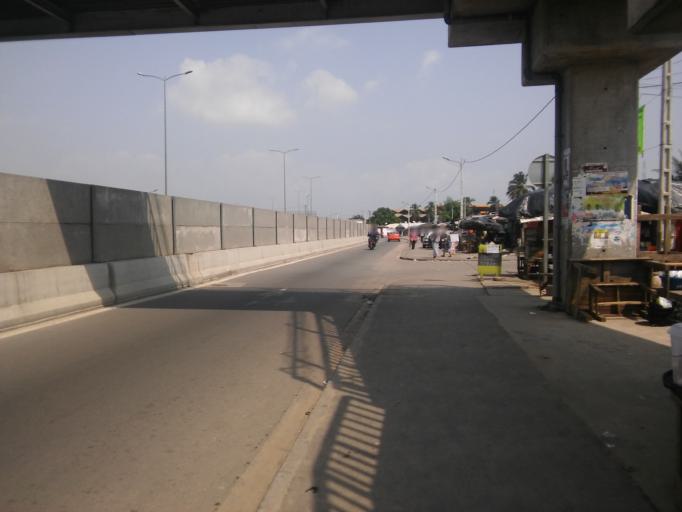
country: CI
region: Lagunes
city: Abidjan
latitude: 5.2986
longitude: -3.9794
